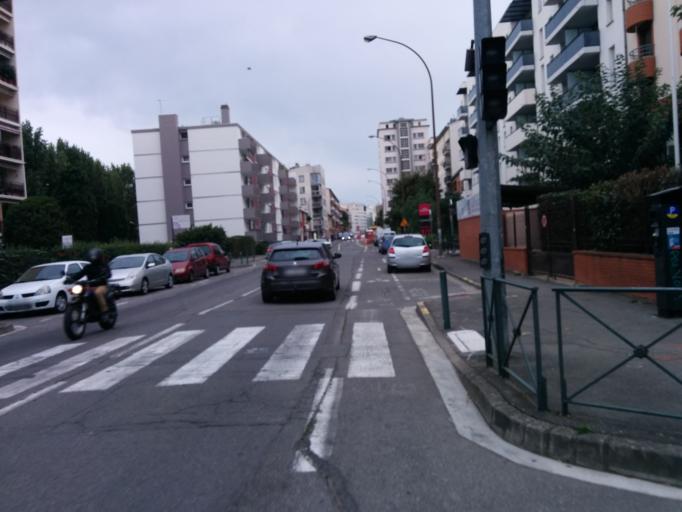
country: FR
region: Midi-Pyrenees
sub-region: Departement de la Haute-Garonne
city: Toulouse
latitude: 43.6019
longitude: 1.4203
